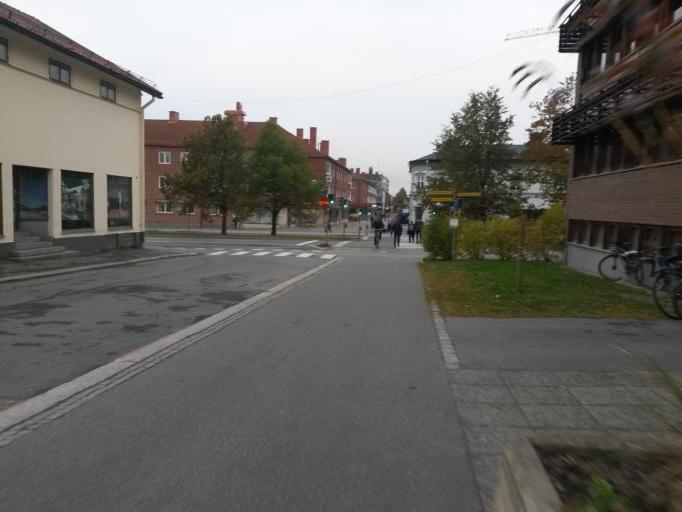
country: SE
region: Vaesterbotten
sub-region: Skelleftea Kommun
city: Skelleftea
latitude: 64.7502
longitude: 20.9616
